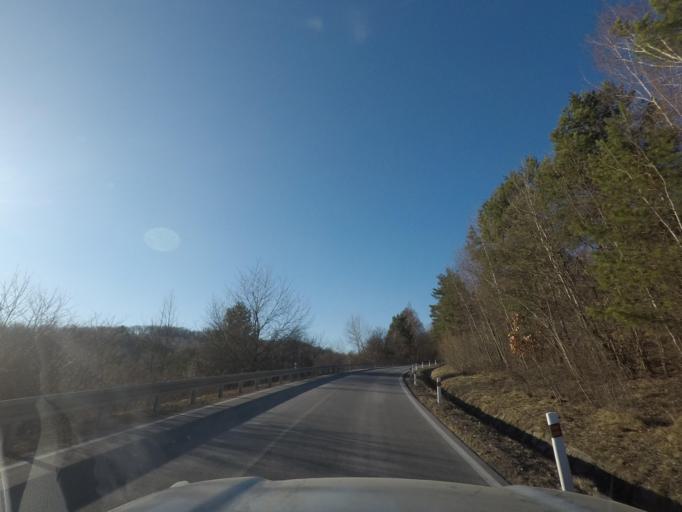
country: SK
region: Presovsky
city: Medzilaborce
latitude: 49.2726
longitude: 21.8639
